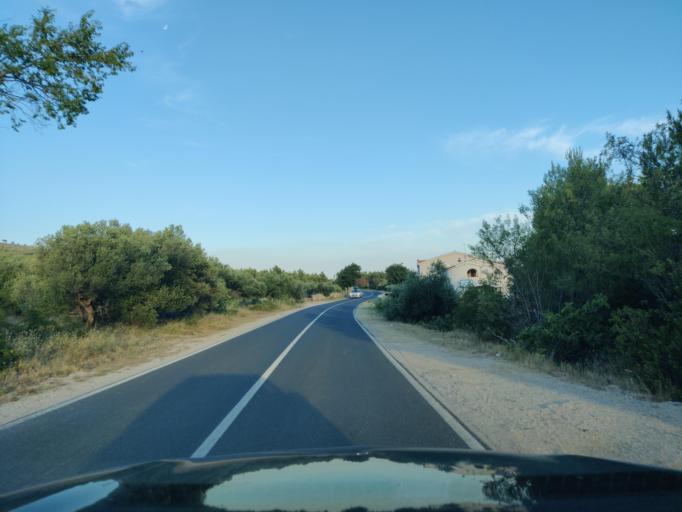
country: HR
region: Sibensko-Kniniska
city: Tribunj
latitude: 43.7672
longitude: 15.7324
